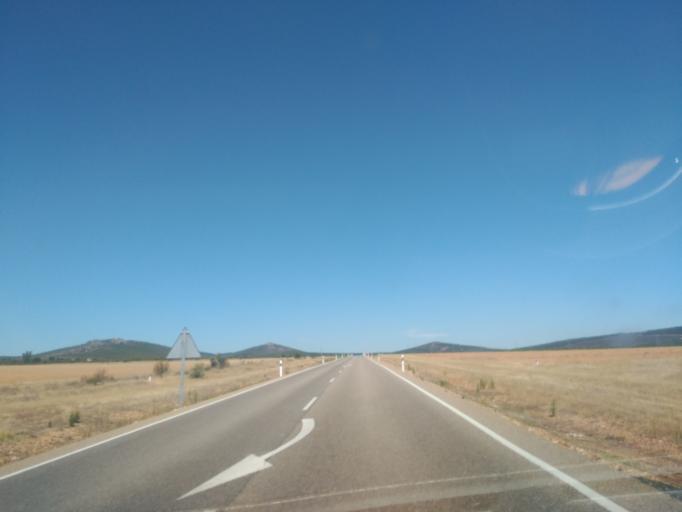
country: ES
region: Castille and Leon
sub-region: Provincia de Zamora
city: Tabara
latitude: 41.8443
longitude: -5.9788
